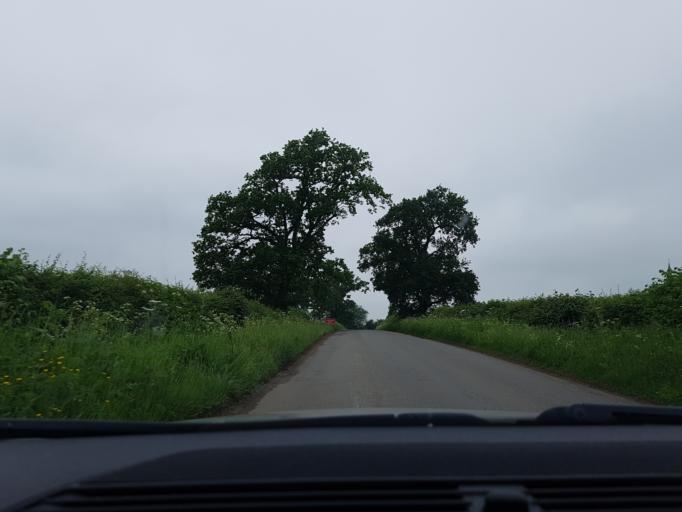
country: GB
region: England
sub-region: Buckinghamshire
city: Steeple Claydon
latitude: 51.9330
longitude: -0.9732
